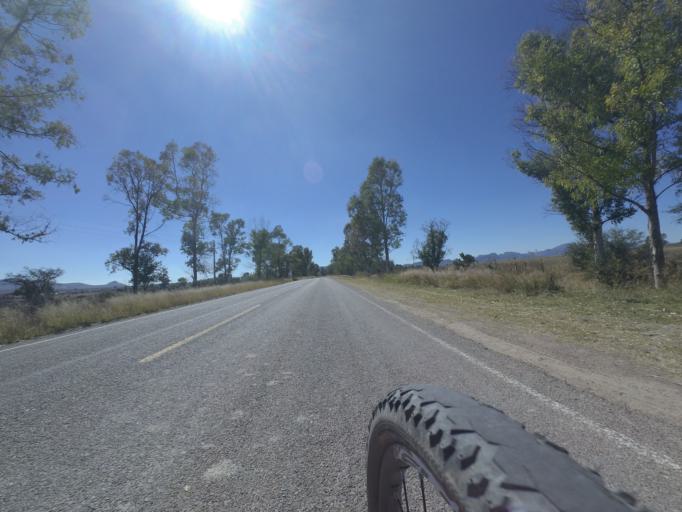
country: MX
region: Aguascalientes
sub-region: Aguascalientes
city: Los Canos
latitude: 21.8809
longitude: -102.4935
